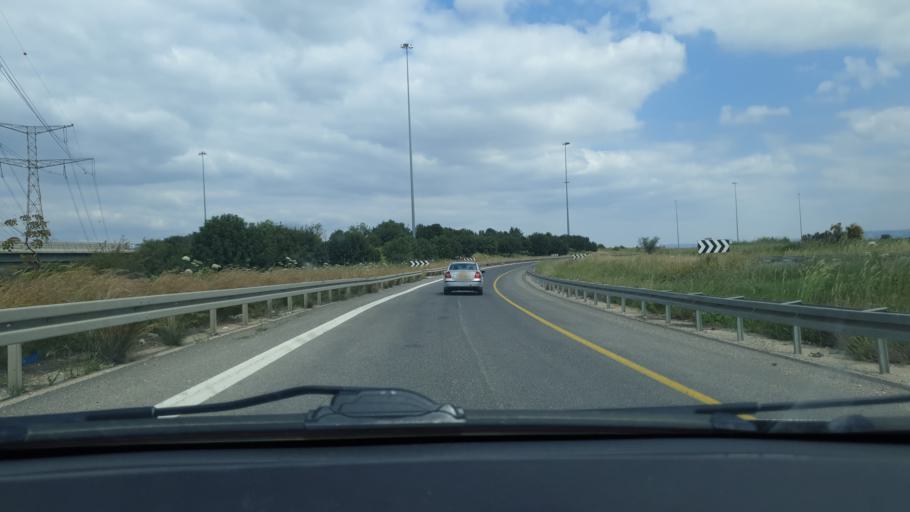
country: IL
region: Central District
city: Lod
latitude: 31.9092
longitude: 34.8989
